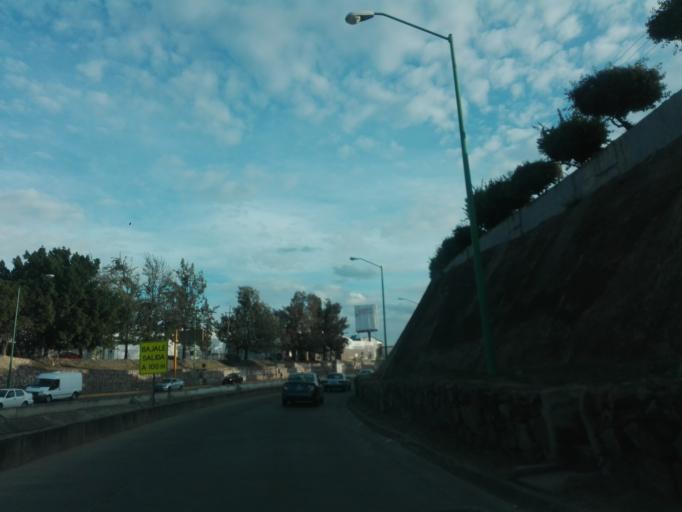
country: MX
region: Guanajuato
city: Leon
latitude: 21.1398
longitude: -101.6802
